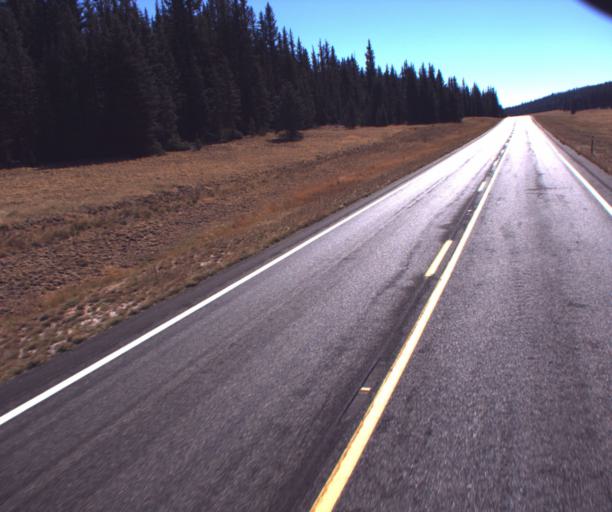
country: US
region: Arizona
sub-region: Coconino County
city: Grand Canyon
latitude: 36.3836
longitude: -112.1262
